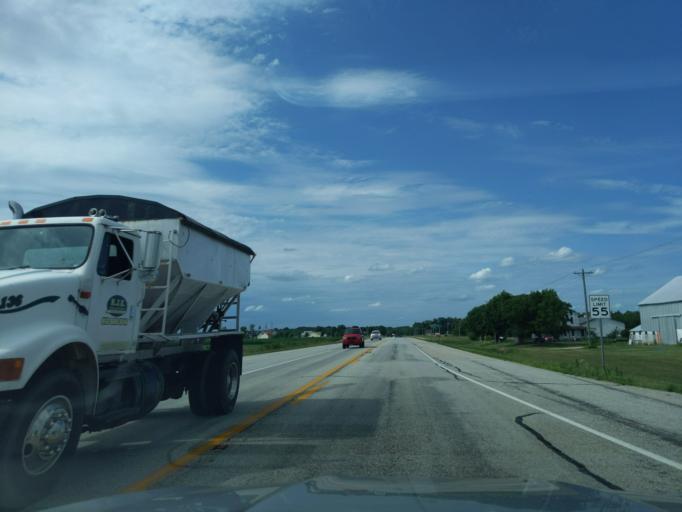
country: US
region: Indiana
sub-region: Ripley County
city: Batesville
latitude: 39.1954
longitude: -85.2076
